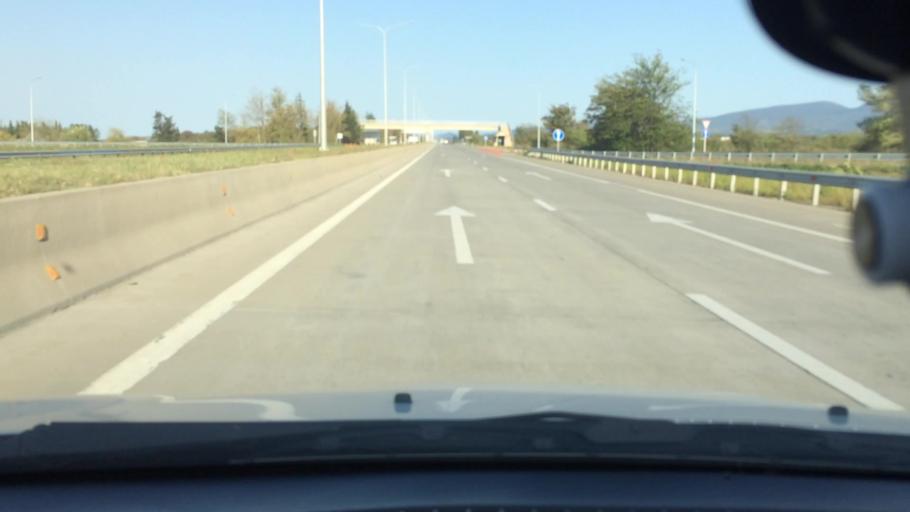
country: GE
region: Imereti
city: Zestap'oni
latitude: 42.1592
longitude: 42.9497
